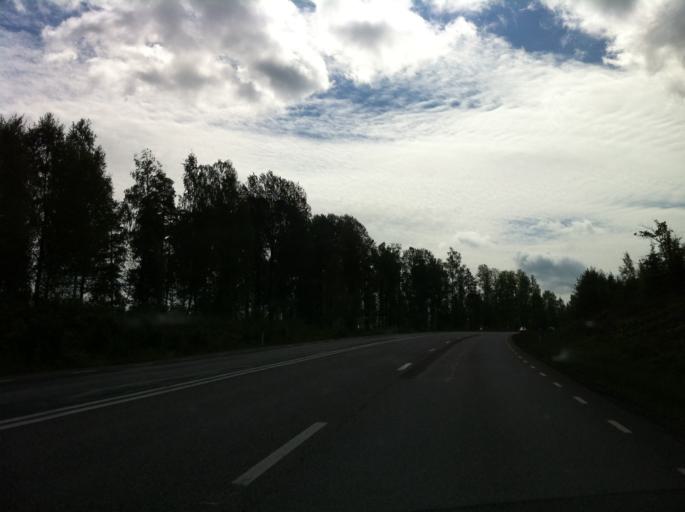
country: SE
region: Vaermland
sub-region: Grums Kommun
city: Slottsbron
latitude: 59.2527
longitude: 13.0030
